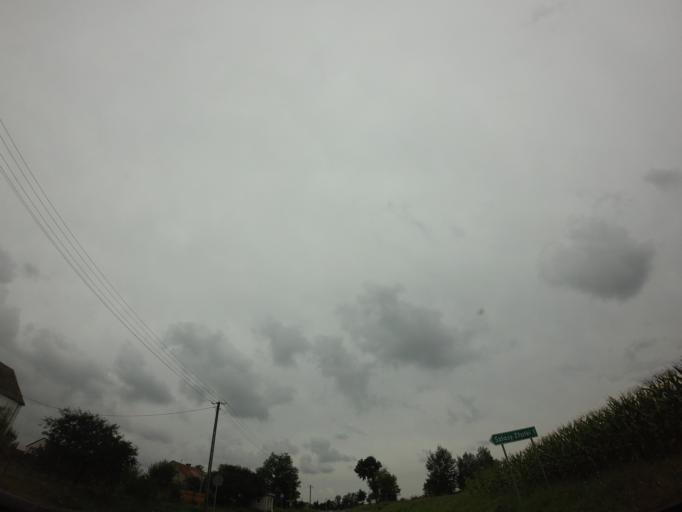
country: PL
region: Masovian Voivodeship
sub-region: Powiat makowski
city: Karniewo
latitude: 52.8429
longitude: 21.0328
